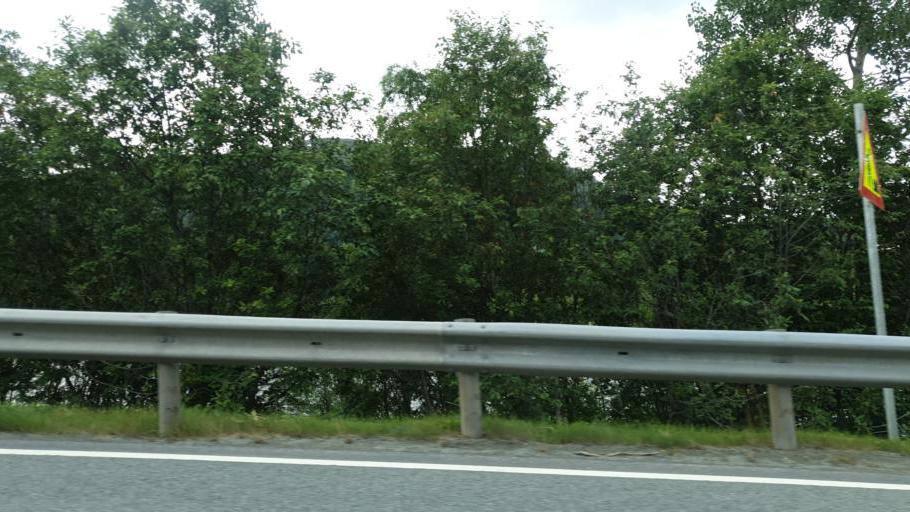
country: NO
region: Sor-Trondelag
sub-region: Oppdal
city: Oppdal
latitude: 62.5527
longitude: 9.6326
